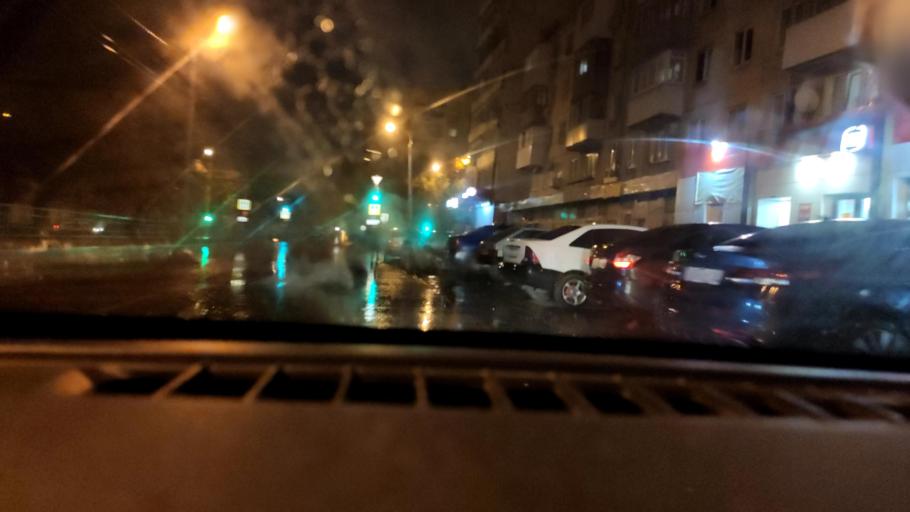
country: RU
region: Samara
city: Samara
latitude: 53.1904
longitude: 50.1743
